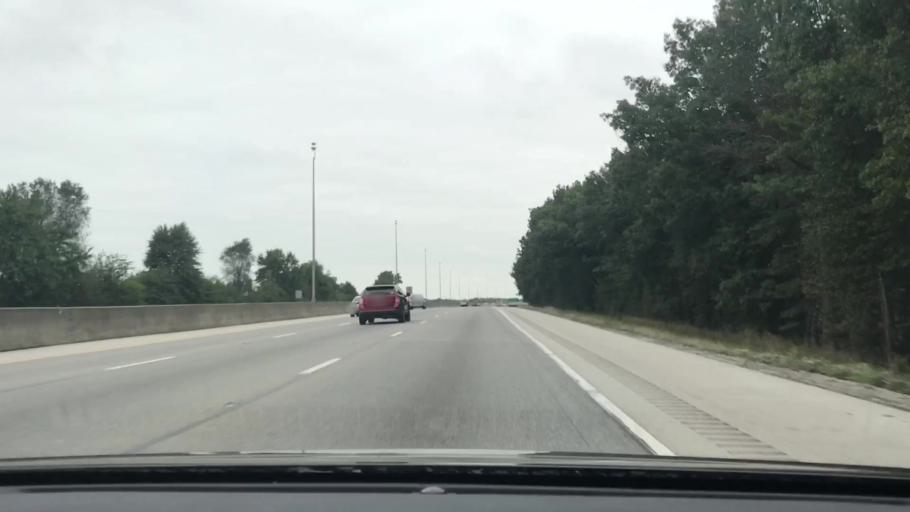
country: US
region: Kentucky
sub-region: Warren County
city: Plano
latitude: 36.8957
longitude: -86.4391
